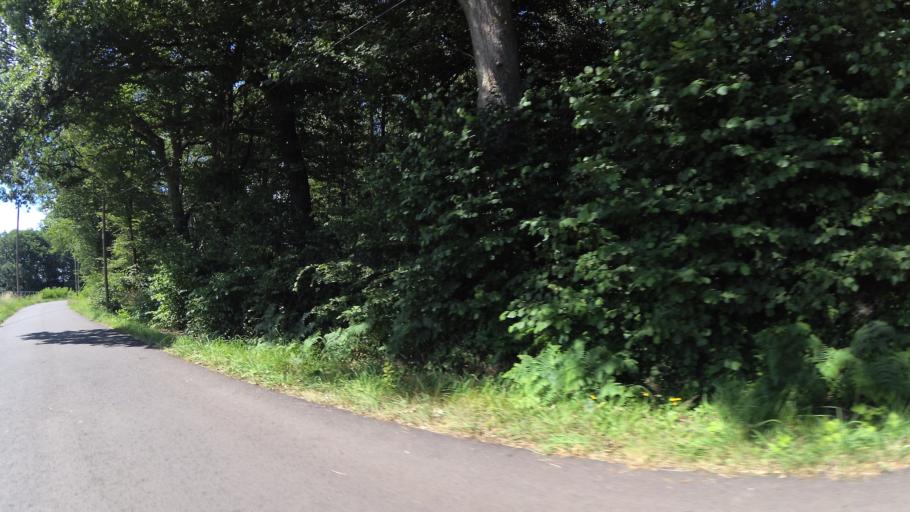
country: DE
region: Saarland
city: Weiskirchen
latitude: 49.5065
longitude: 6.8212
